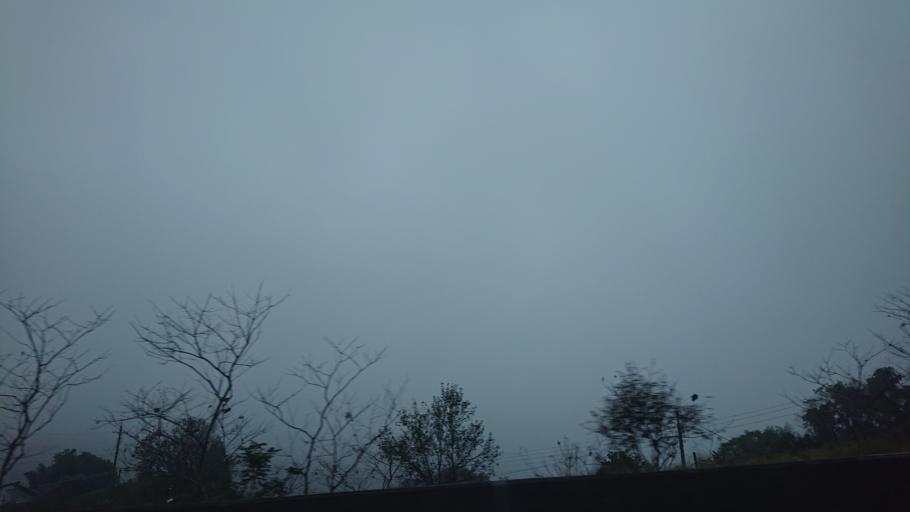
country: TW
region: Taiwan
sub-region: Chiayi
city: Jiayi Shi
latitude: 23.4758
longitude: 120.6968
